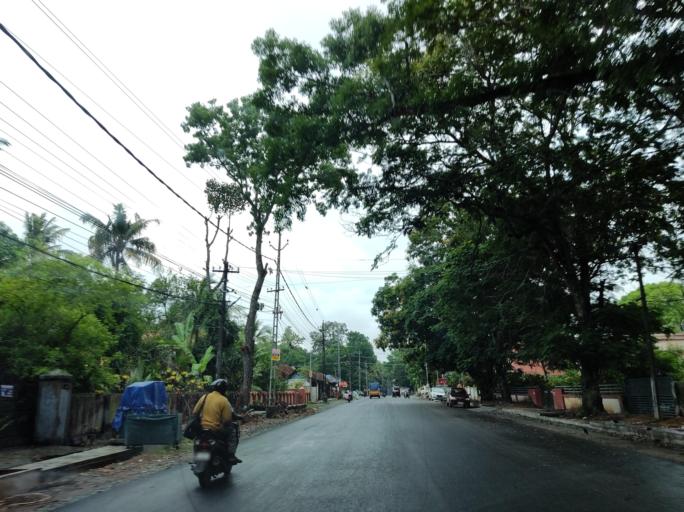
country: IN
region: Kerala
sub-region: Alappuzha
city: Mavelikara
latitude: 9.2507
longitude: 76.5270
